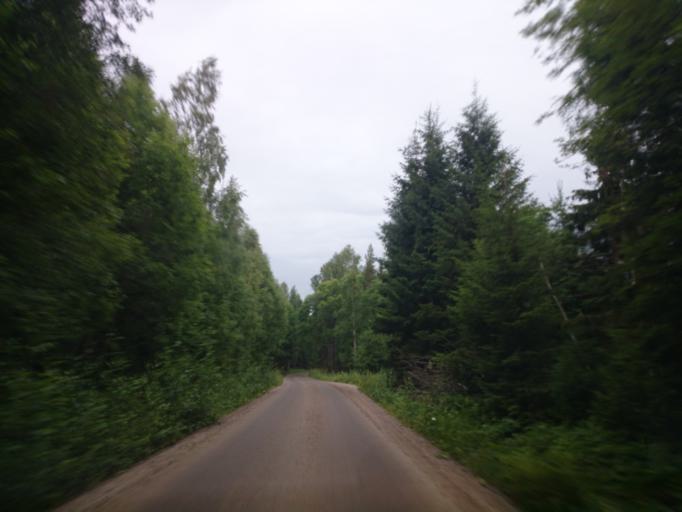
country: SE
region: Vaesternorrland
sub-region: Sundsvalls Kommun
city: Njurundabommen
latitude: 62.1379
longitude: 17.4162
